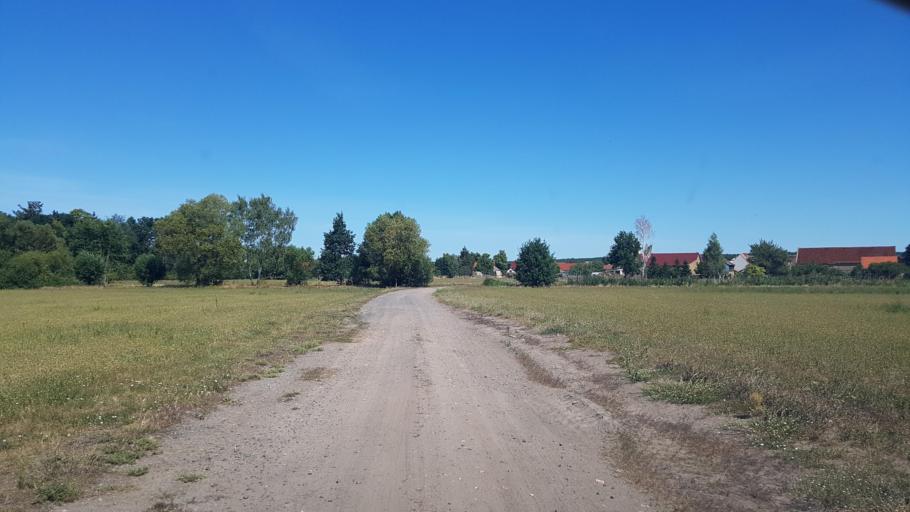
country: DE
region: Brandenburg
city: Golzow
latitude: 52.2536
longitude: 12.6626
